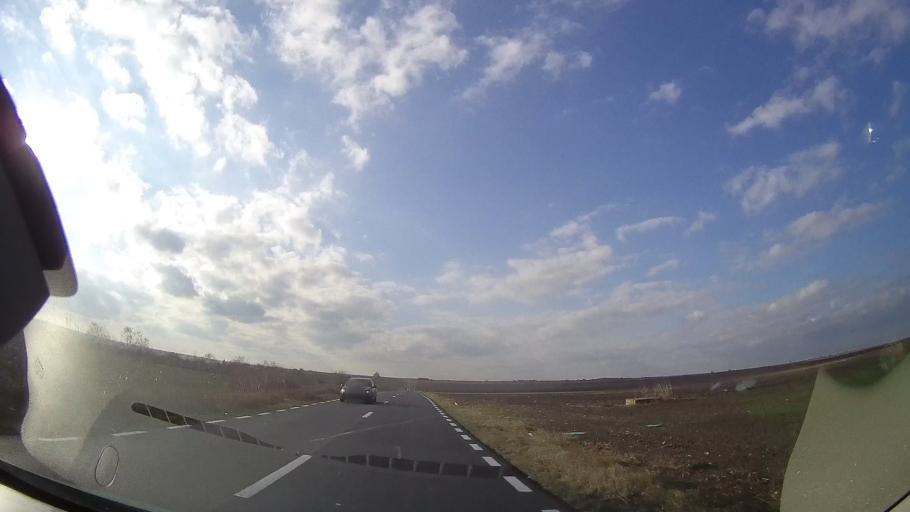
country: RO
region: Constanta
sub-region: Comuna Limanu
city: Limanu
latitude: 43.8244
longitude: 28.5072
